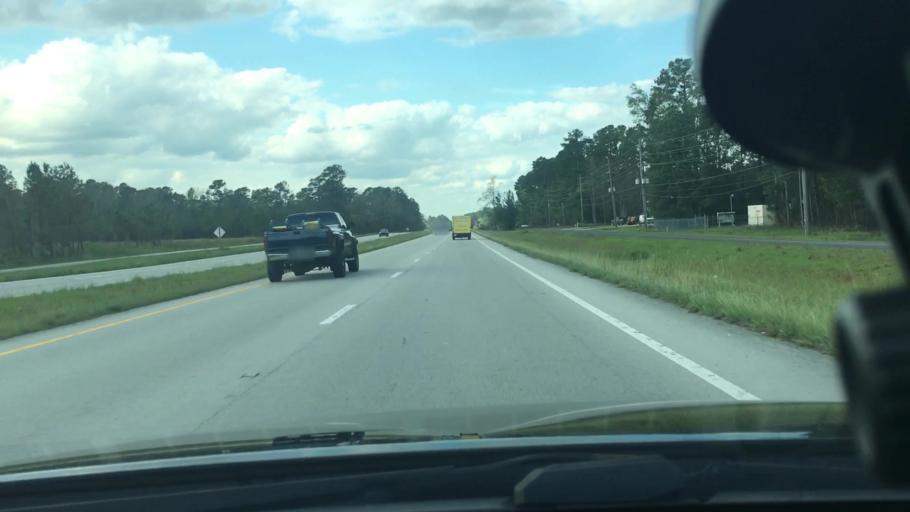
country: US
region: North Carolina
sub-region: Craven County
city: Neuse Forest
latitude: 34.9989
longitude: -76.9858
